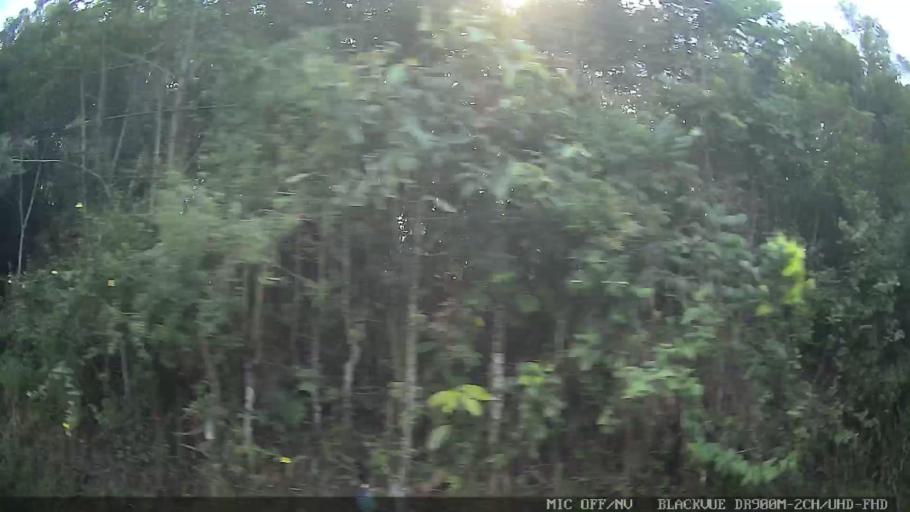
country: BR
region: Sao Paulo
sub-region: Mogi das Cruzes
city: Mogi das Cruzes
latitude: -23.6845
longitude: -46.2150
